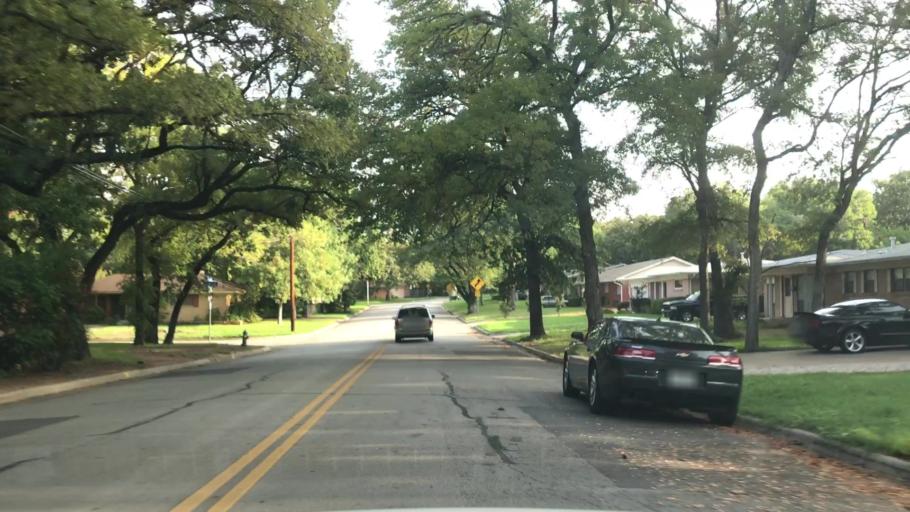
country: US
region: Texas
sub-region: Tarrant County
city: Arlington
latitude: 32.7447
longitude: -97.1233
